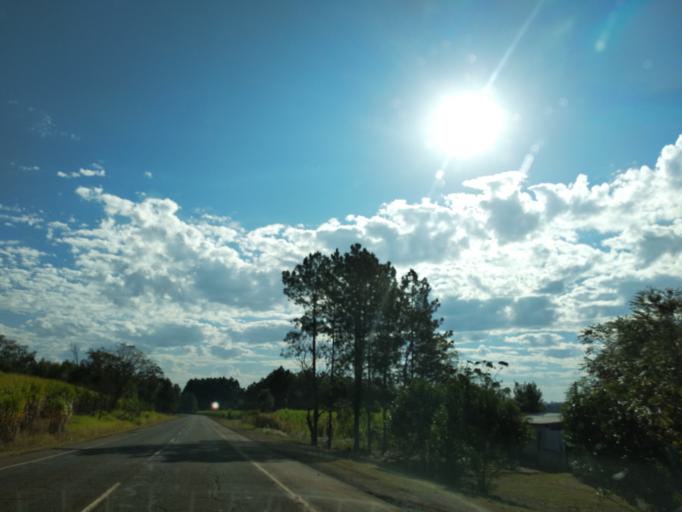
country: AR
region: Misiones
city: Ruiz de Montoya
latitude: -27.0605
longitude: -55.0006
